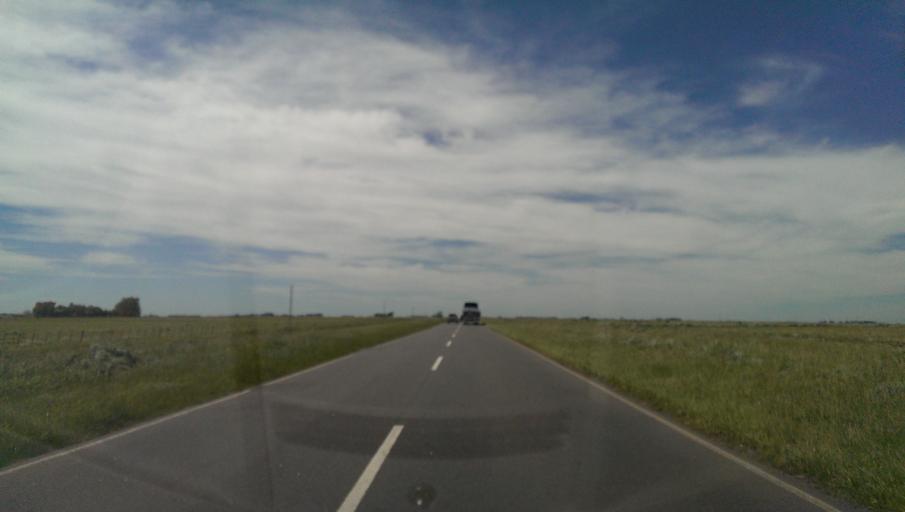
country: AR
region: Buenos Aires
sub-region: Partido de Laprida
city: Laprida
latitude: -37.2434
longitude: -60.7902
